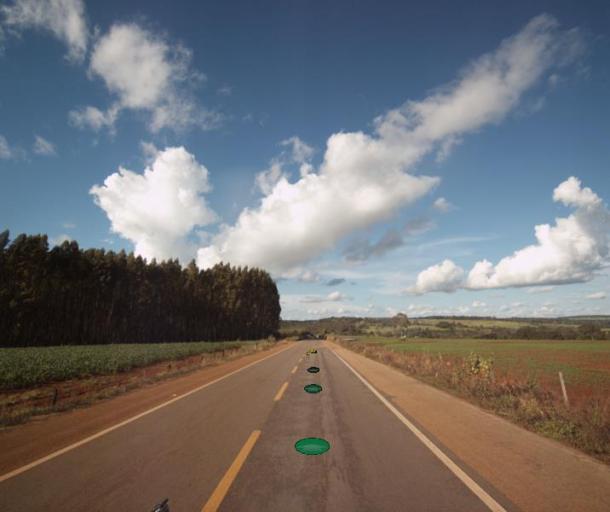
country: BR
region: Goias
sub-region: Itaberai
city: Itaberai
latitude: -16.0056
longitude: -49.7569
